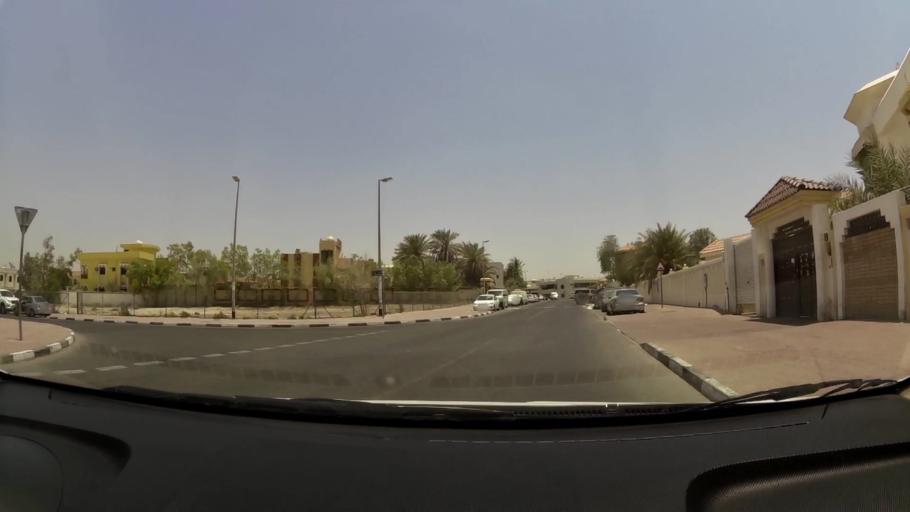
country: AE
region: Ash Shariqah
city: Sharjah
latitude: 25.2880
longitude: 55.3299
